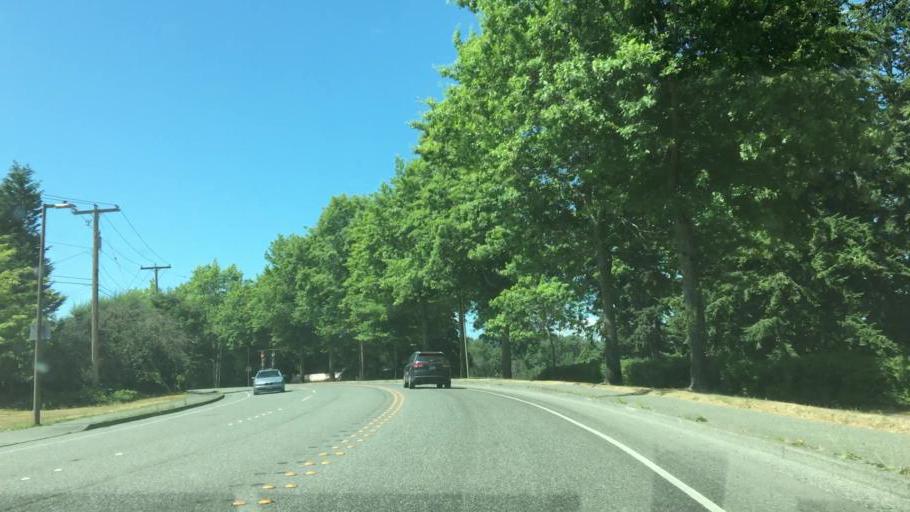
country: US
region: Washington
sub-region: Whatcom County
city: Geneva
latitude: 48.7478
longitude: -122.4400
